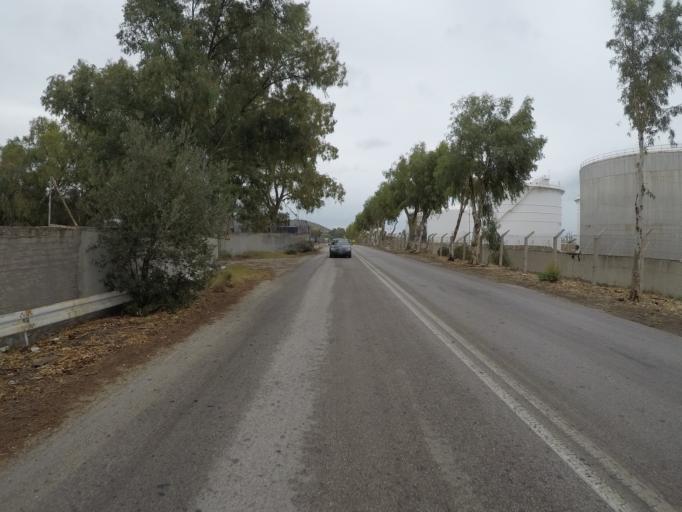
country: GR
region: Peloponnese
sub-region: Nomos Korinthias
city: Agioi Theodoroi
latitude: 37.9196
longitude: 23.0804
